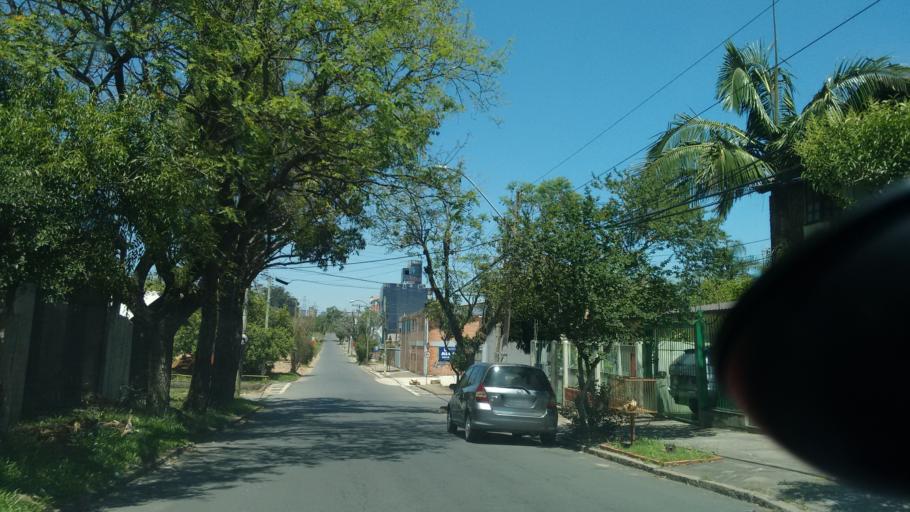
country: BR
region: Rio Grande do Sul
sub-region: Cachoeirinha
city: Cachoeirinha
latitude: -29.9981
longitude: -51.1257
